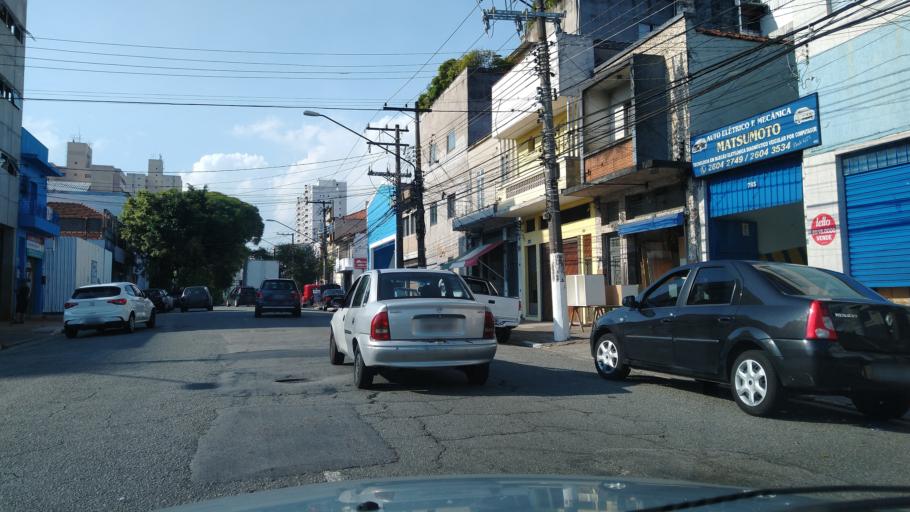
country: BR
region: Sao Paulo
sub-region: Sao Paulo
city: Sao Paulo
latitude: -23.5655
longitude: -46.6008
